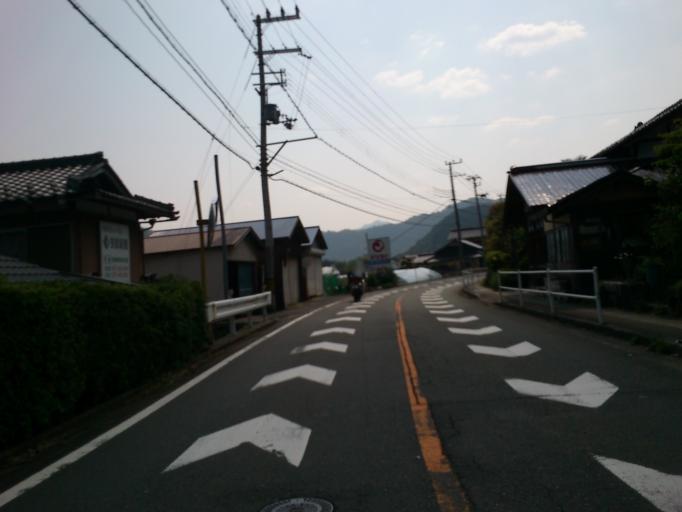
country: JP
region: Fukui
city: Obama
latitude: 35.2772
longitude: 135.5863
